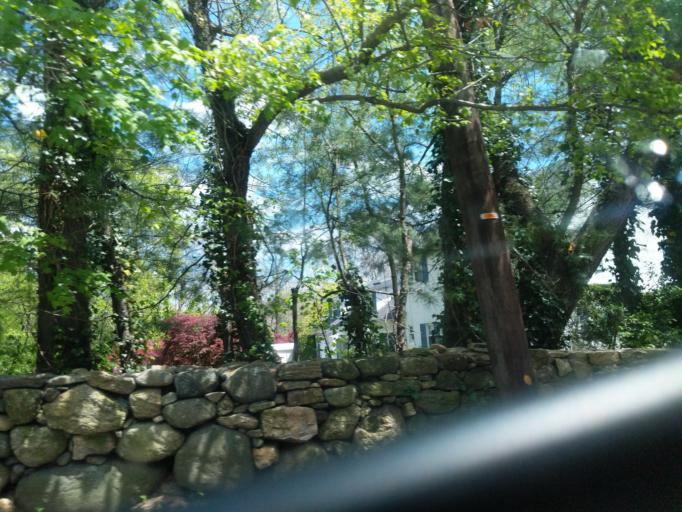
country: US
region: New York
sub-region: Westchester County
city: Tuckahoe
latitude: 40.9568
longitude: -73.7948
